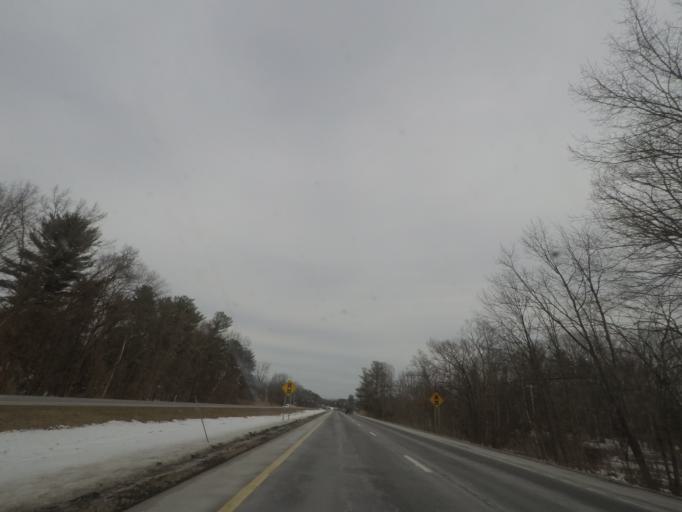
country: US
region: New York
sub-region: Albany County
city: Delmar
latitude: 42.6055
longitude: -73.8383
